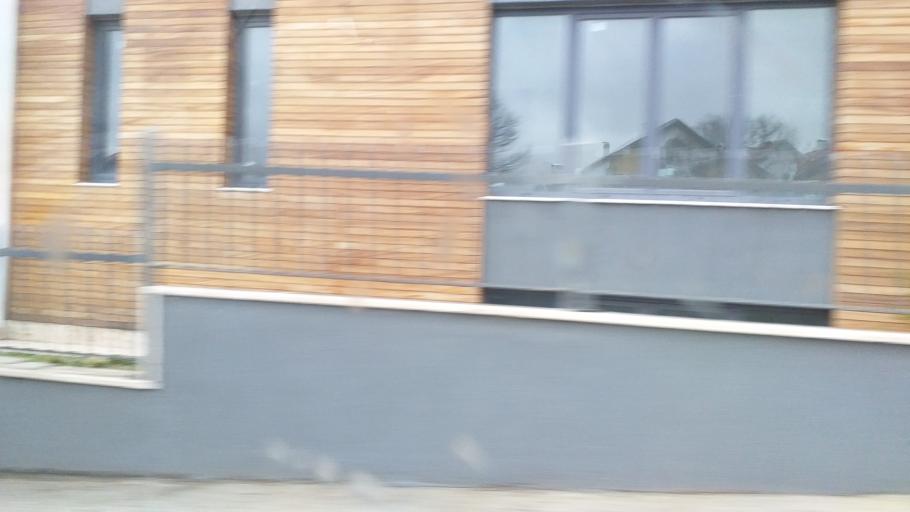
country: TR
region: Ankara
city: Batikent
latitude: 39.8762
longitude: 32.7144
